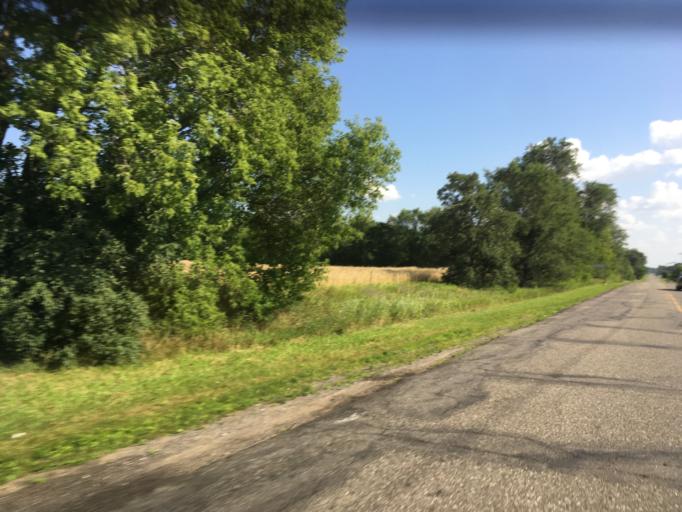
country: US
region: Minnesota
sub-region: Stearns County
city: Sartell
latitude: 45.6625
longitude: -94.2223
